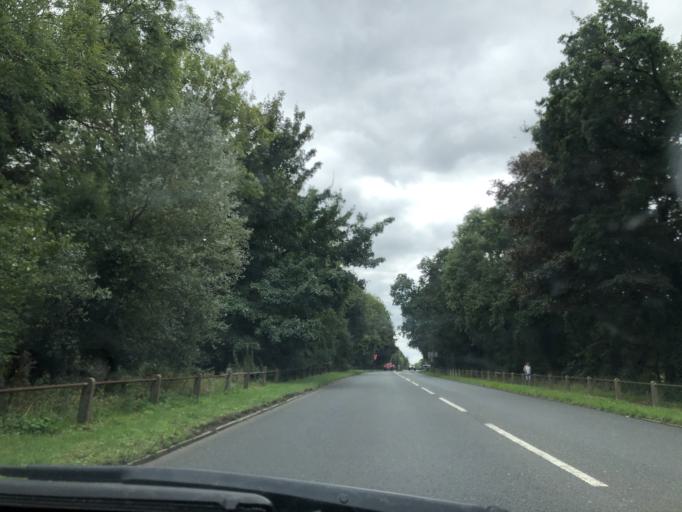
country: GB
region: England
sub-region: Greater London
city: Orpington
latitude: 51.3599
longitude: 0.1200
